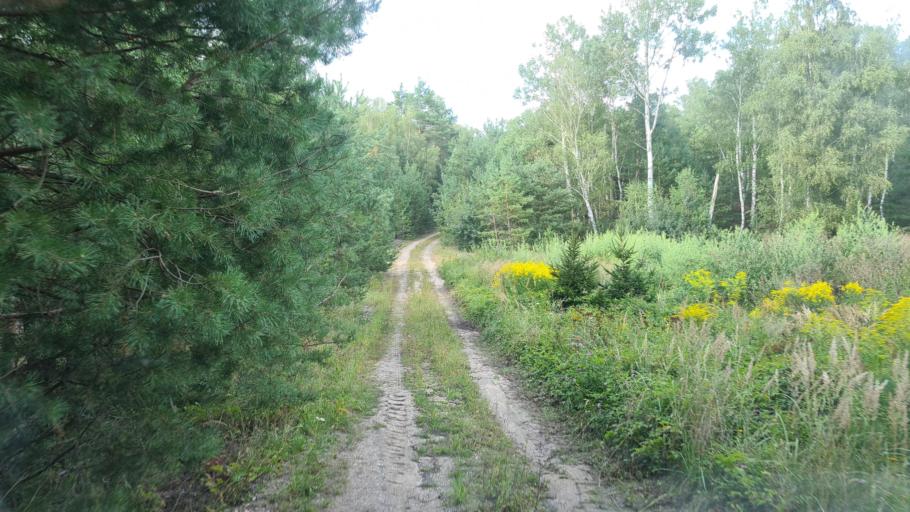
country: DE
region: Brandenburg
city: Schonborn
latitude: 51.6063
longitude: 13.4725
